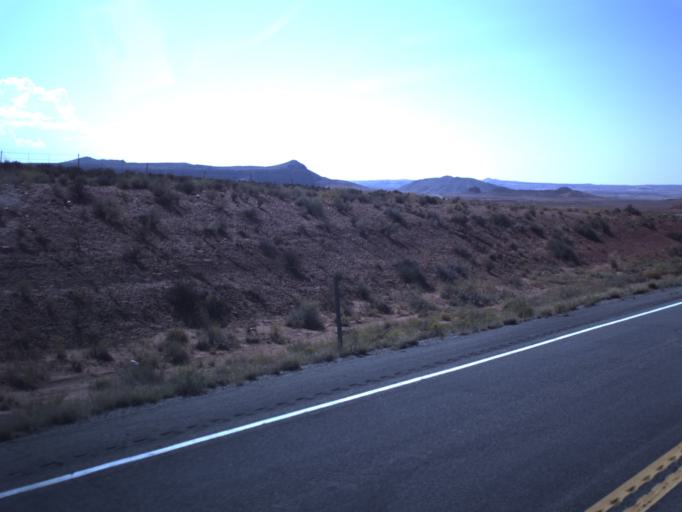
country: US
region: Utah
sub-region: San Juan County
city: Blanding
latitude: 37.0146
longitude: -109.6119
